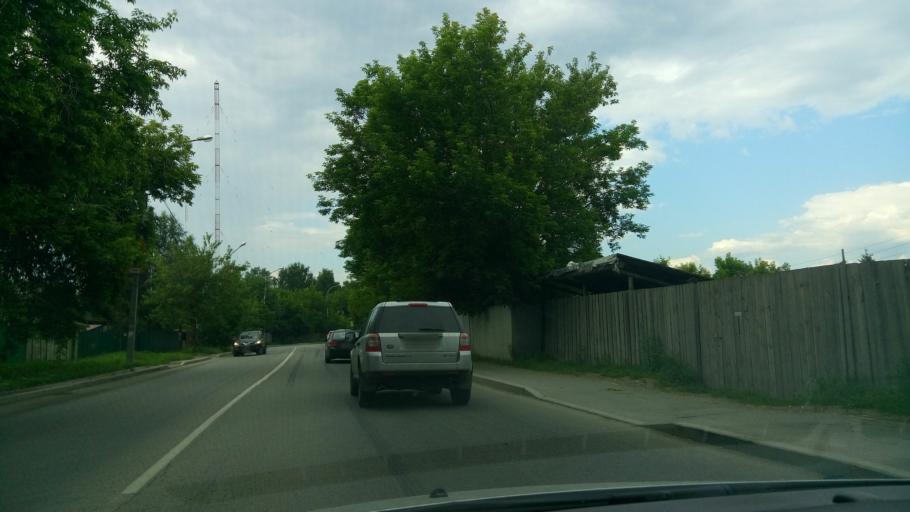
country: RU
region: Sverdlovsk
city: Yekaterinburg
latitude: 56.8803
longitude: 60.6929
